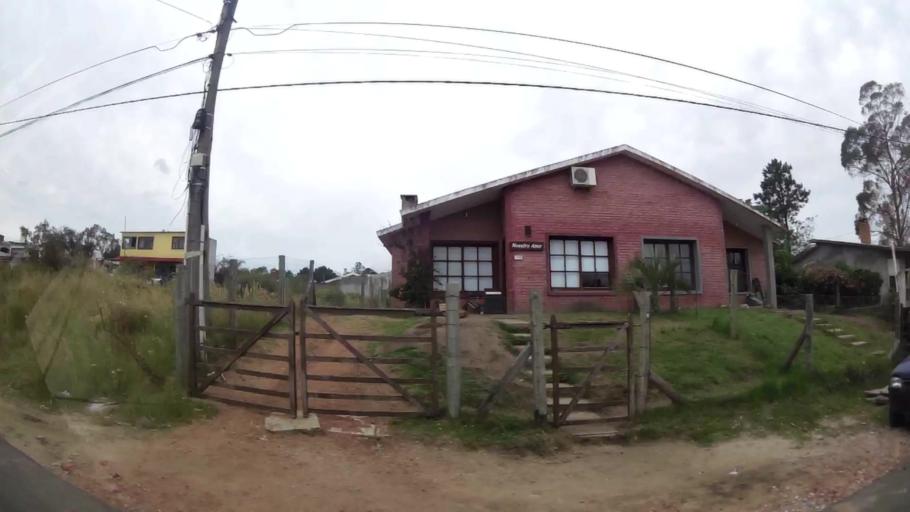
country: UY
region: Maldonado
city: Maldonado
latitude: -34.9045
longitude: -54.9740
